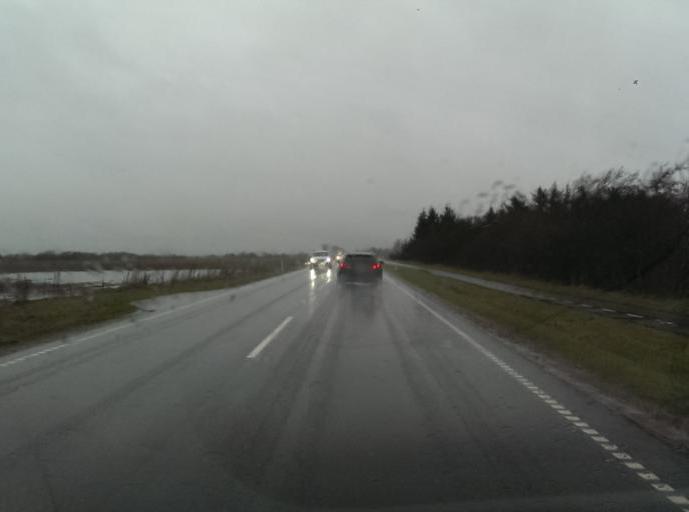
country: DK
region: South Denmark
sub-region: Varde Kommune
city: Olgod
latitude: 55.7384
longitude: 8.6177
